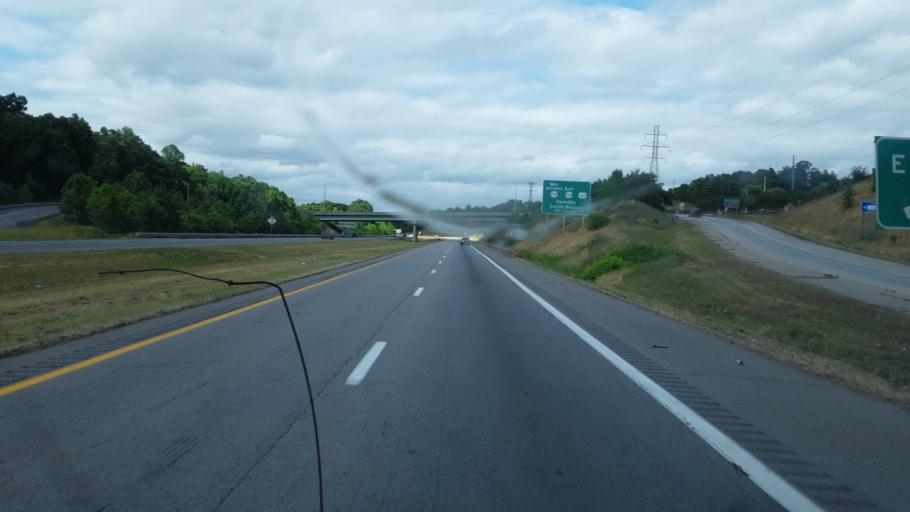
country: US
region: Virginia
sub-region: City of Danville
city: Danville
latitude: 36.5721
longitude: -79.3689
